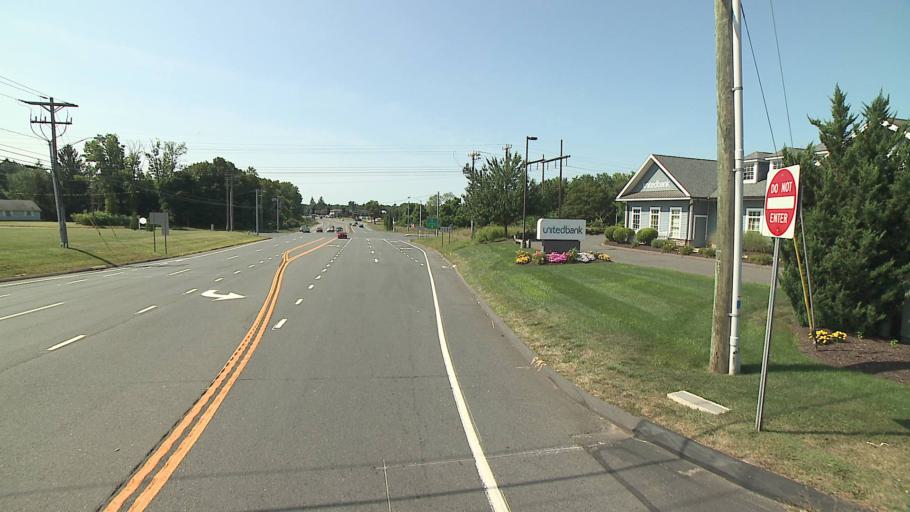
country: US
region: Connecticut
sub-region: Hartford County
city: Windsor Locks
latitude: 41.9180
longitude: -72.6104
